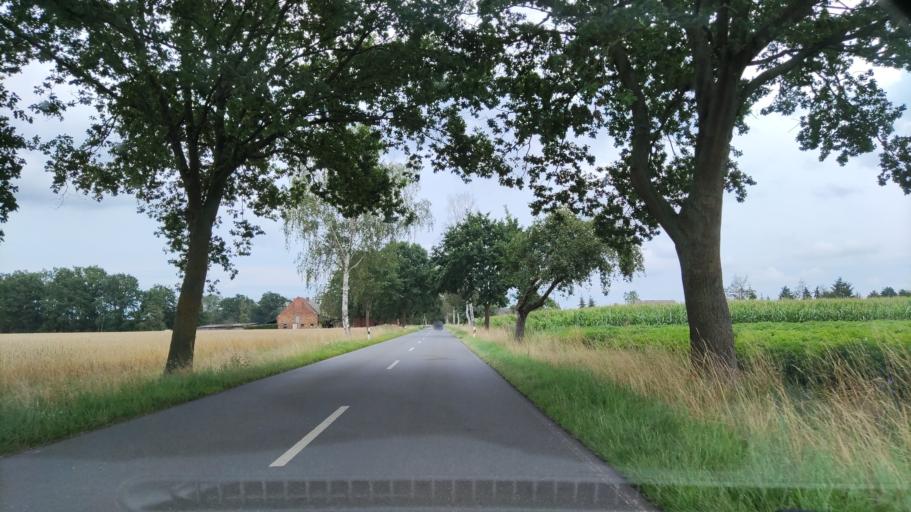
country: DE
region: Lower Saxony
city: Klein Gusborn
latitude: 53.0523
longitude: 11.1510
